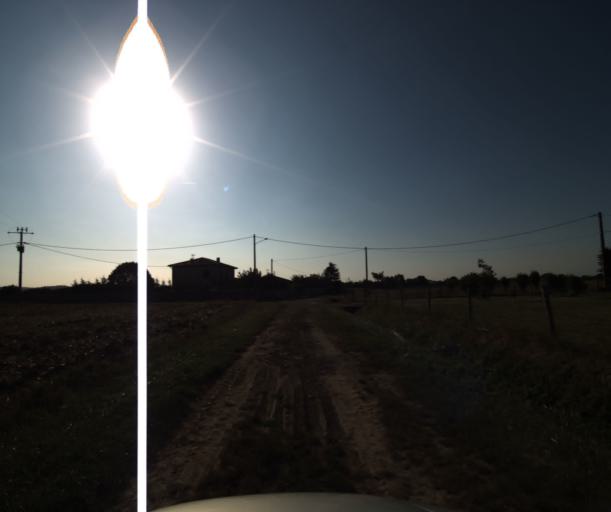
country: FR
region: Midi-Pyrenees
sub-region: Departement de la Haute-Garonne
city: Labarthe-sur-Leze
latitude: 43.4521
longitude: 1.3776
